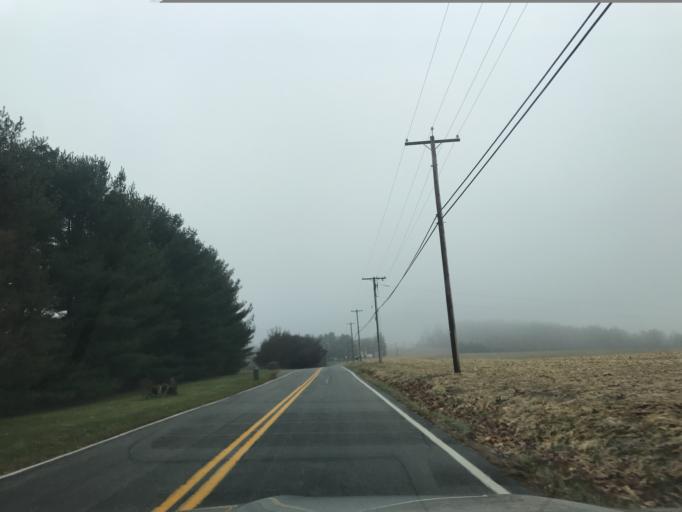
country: US
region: Maryland
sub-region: Harford County
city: South Bel Air
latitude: 39.5821
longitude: -76.2814
